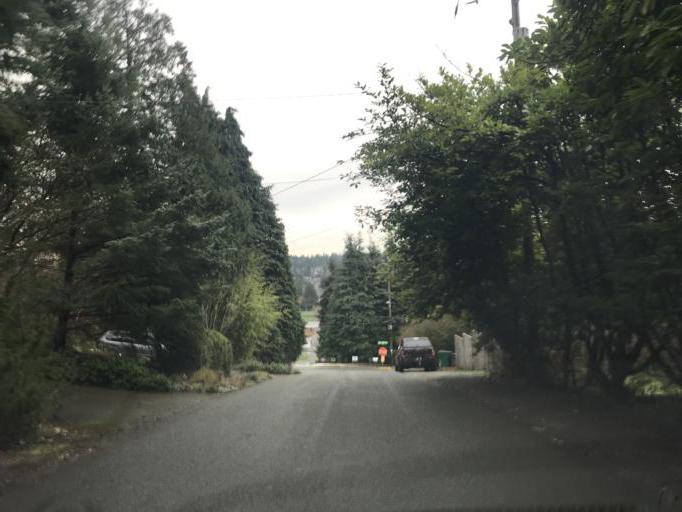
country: US
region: Washington
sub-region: King County
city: Lake Forest Park
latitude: 47.7089
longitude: -122.2854
